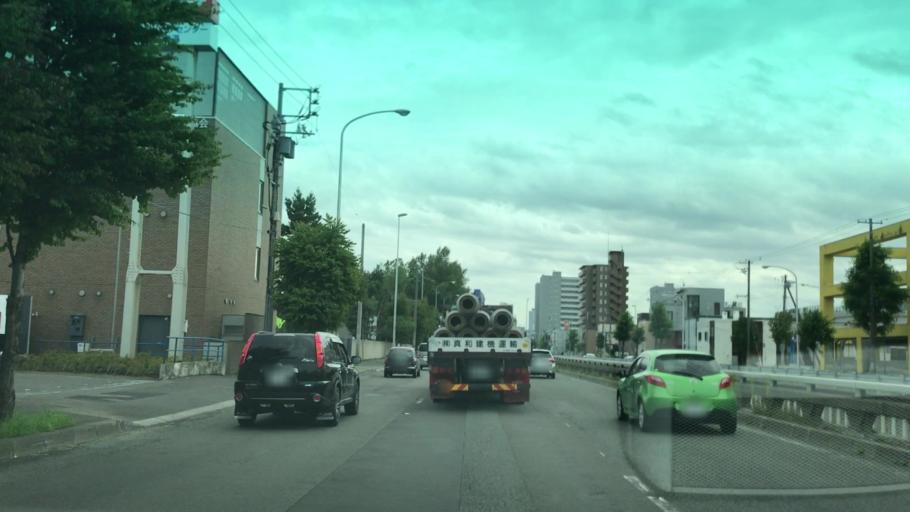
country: JP
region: Hokkaido
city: Sapporo
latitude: 43.0969
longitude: 141.3461
